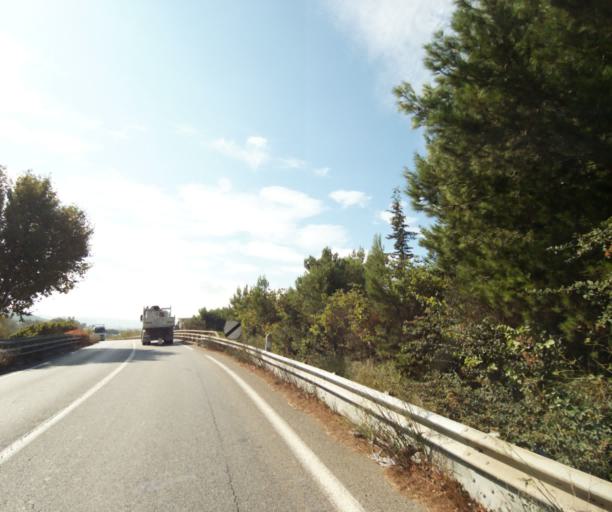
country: FR
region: Provence-Alpes-Cote d'Azur
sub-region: Departement des Bouches-du-Rhone
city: Saint-Victoret
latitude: 43.4214
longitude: 5.2287
